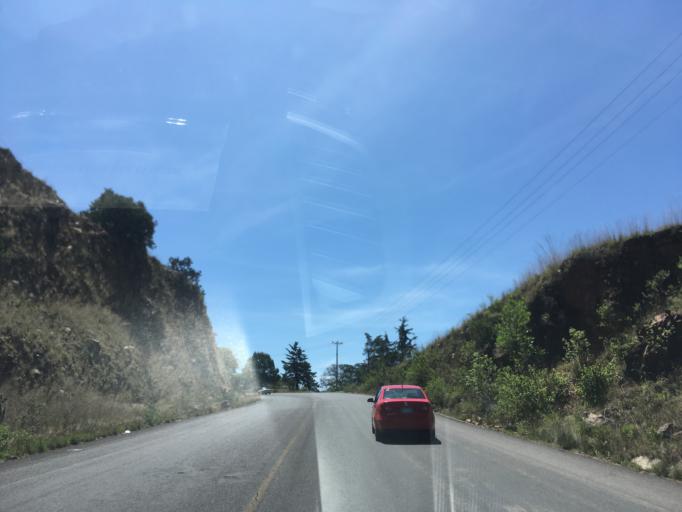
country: MX
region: Michoacan
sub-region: Hidalgo
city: Rincon de Cedenos (Rincon de Dolores)
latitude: 19.6985
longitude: -100.5822
